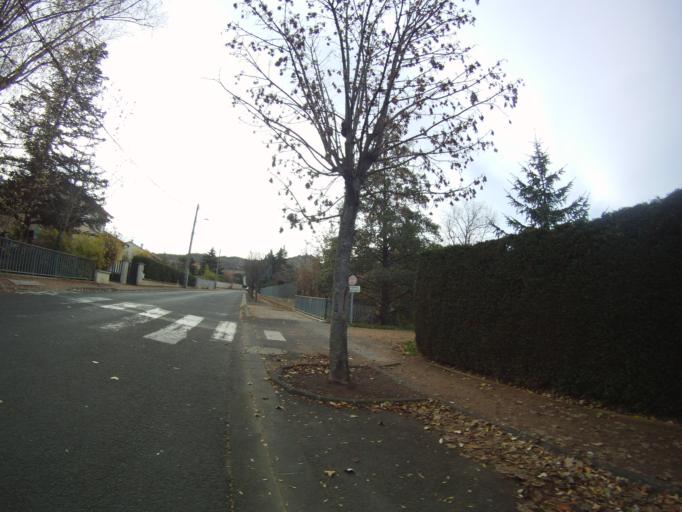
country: FR
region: Auvergne
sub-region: Departement du Puy-de-Dome
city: Beaumont
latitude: 45.7462
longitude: 3.0819
